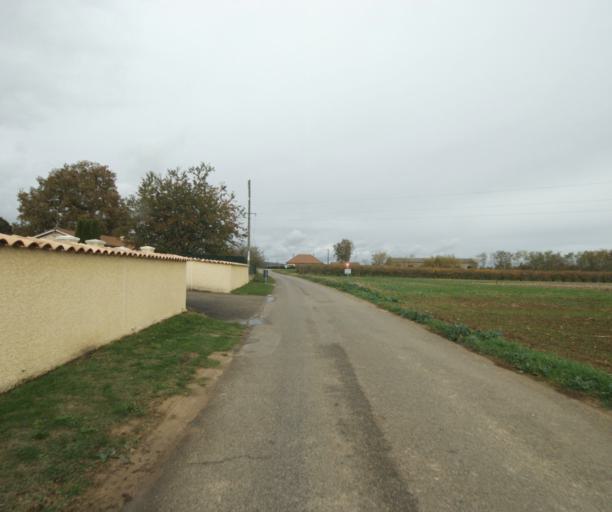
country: FR
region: Rhone-Alpes
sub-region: Departement de l'Ain
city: Pont-de-Vaux
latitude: 46.4640
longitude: 4.8879
